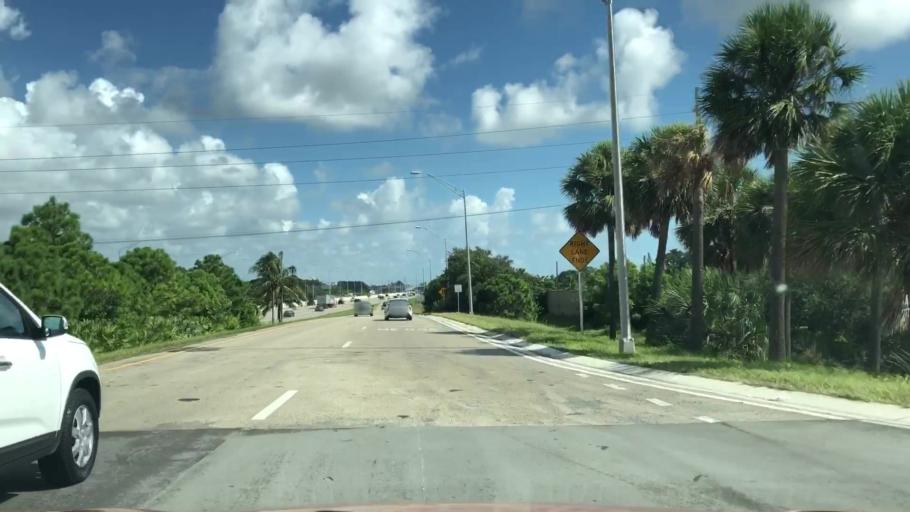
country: US
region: Florida
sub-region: Palm Beach County
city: Hypoluxo
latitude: 26.5725
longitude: -80.0687
